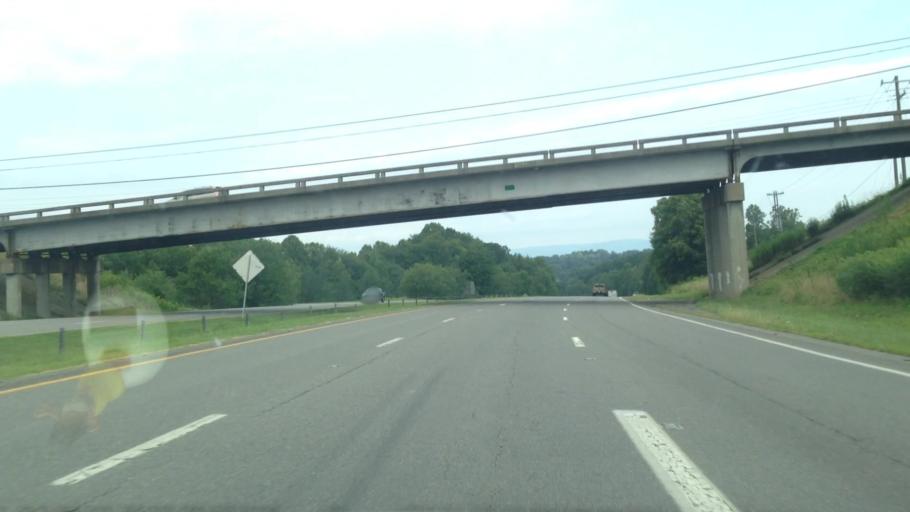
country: US
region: North Carolina
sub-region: Surry County
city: Flat Rock
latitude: 36.4599
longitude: -80.5609
